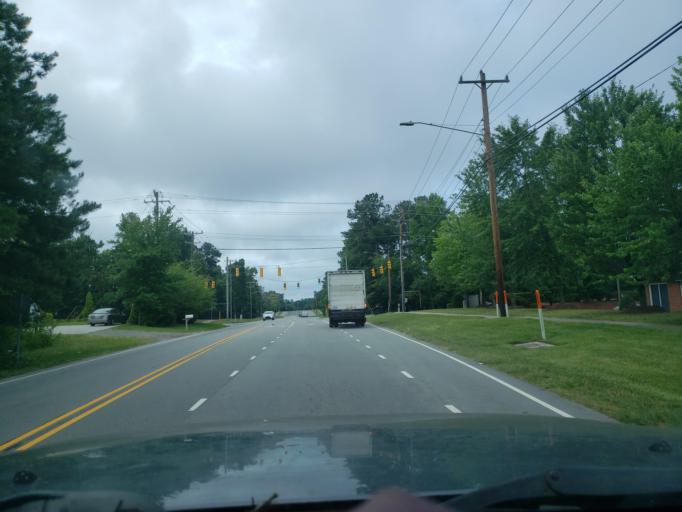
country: US
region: North Carolina
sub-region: Wake County
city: Morrisville
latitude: 35.9268
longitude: -78.8129
